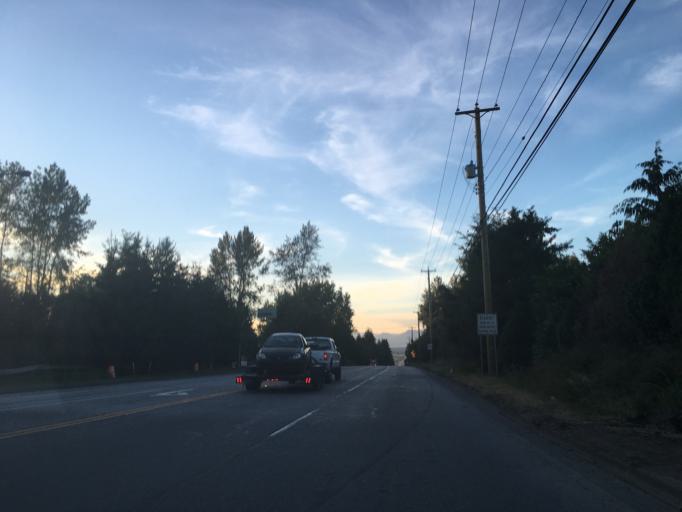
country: US
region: Washington
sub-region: Whatcom County
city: Blaine
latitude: 49.0458
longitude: -122.7352
